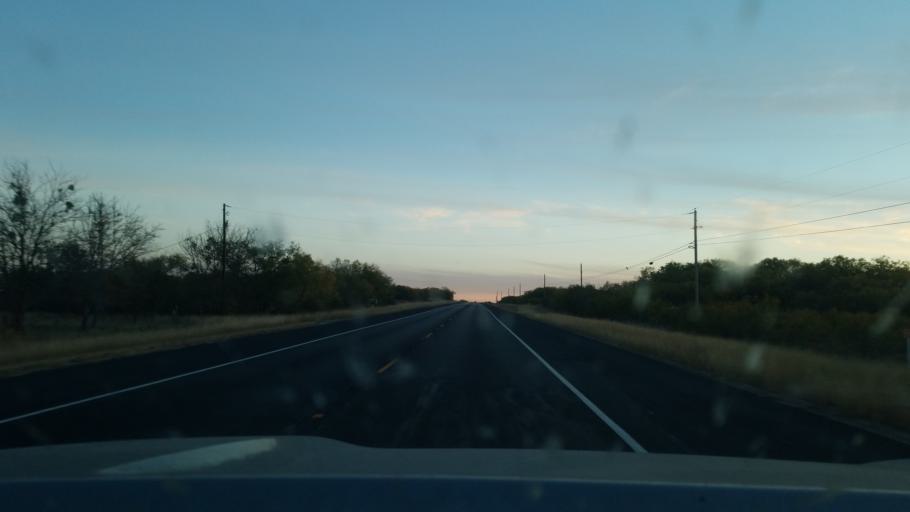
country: US
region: Texas
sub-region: Stephens County
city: Breckenridge
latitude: 32.6460
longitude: -98.9026
